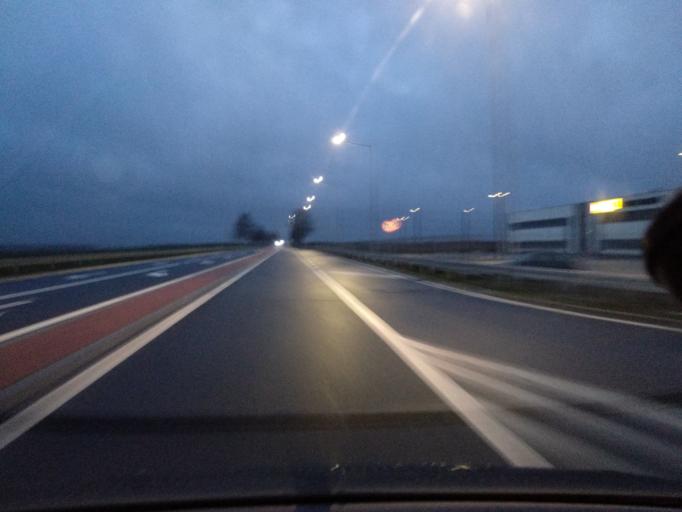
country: PL
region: Lower Silesian Voivodeship
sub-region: Powiat sredzki
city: Miekinia
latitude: 51.1604
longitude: 16.7119
